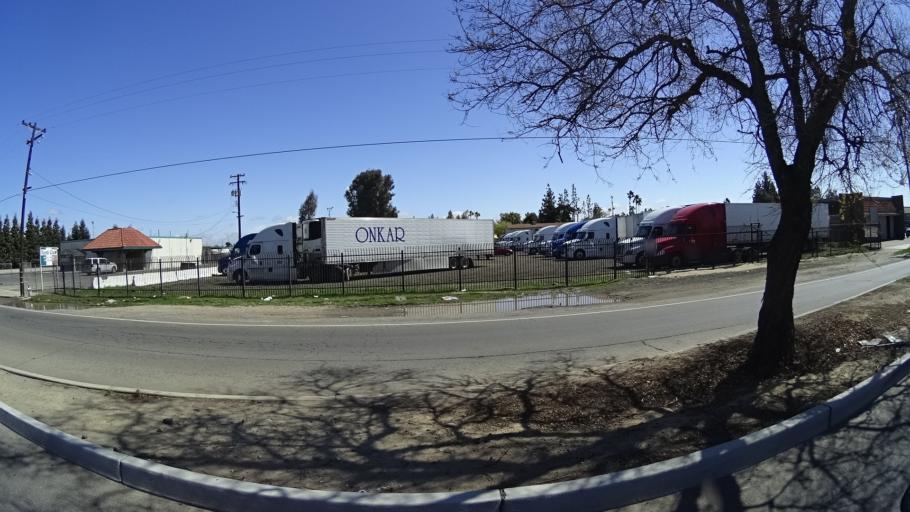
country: US
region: California
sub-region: Fresno County
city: West Park
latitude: 36.7739
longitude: -119.8444
